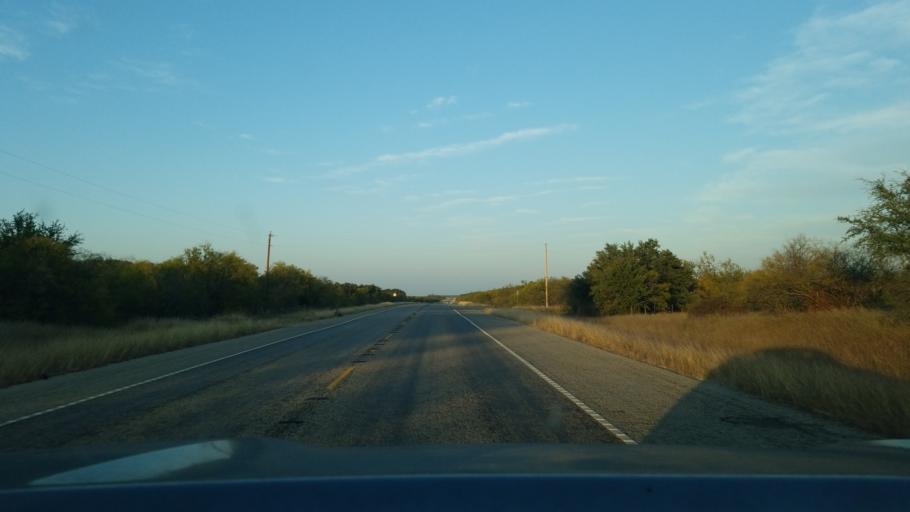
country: US
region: Texas
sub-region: Eastland County
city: Cisco
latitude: 32.4412
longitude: -98.9164
